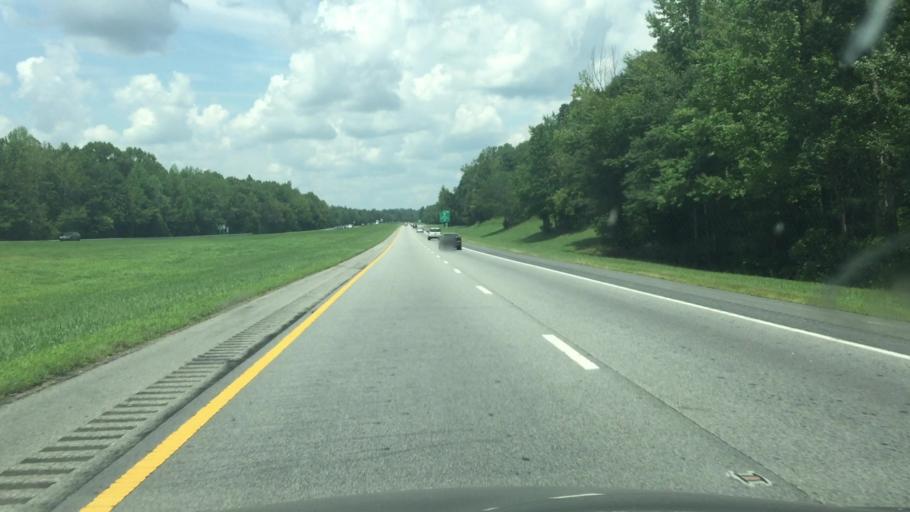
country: US
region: North Carolina
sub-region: Guilford County
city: Pleasant Garden
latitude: 35.9135
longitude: -79.8226
